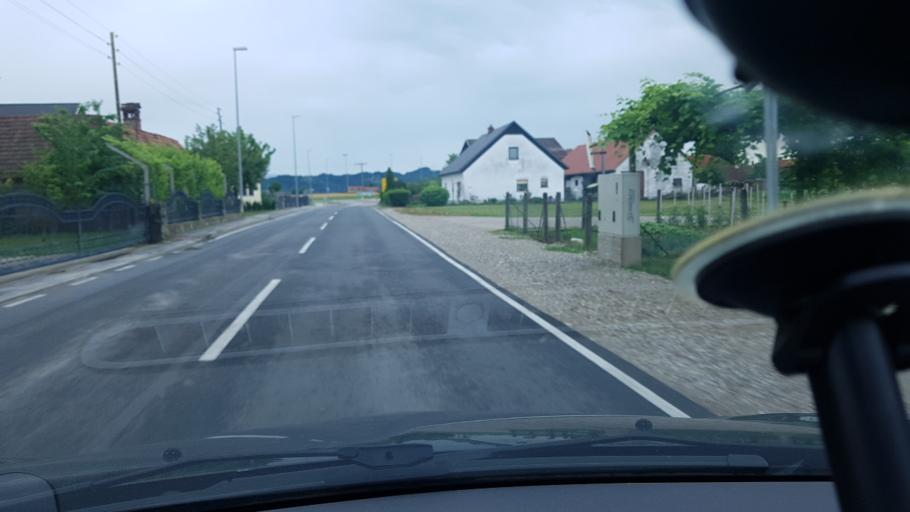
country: SI
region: Hajdina
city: Spodnja Hajdina
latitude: 46.3910
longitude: 15.8683
